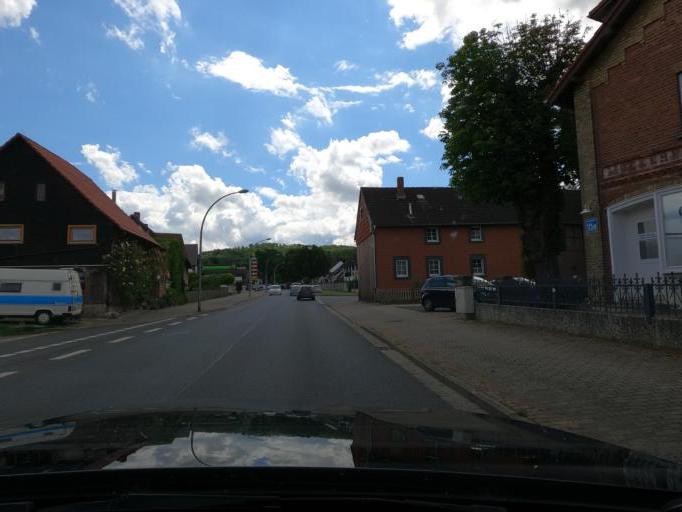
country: DE
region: Lower Saxony
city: Elbe
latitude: 52.1316
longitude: 10.2915
